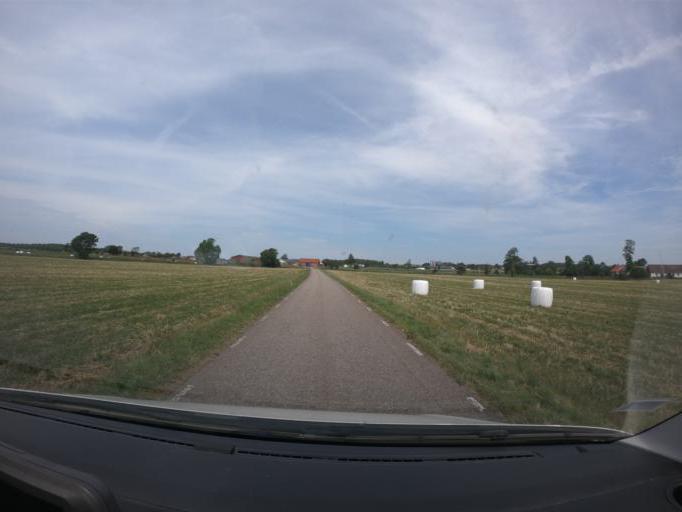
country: SE
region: Skane
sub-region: Angelholms Kommun
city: Vejbystrand
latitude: 56.3744
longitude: 12.7387
